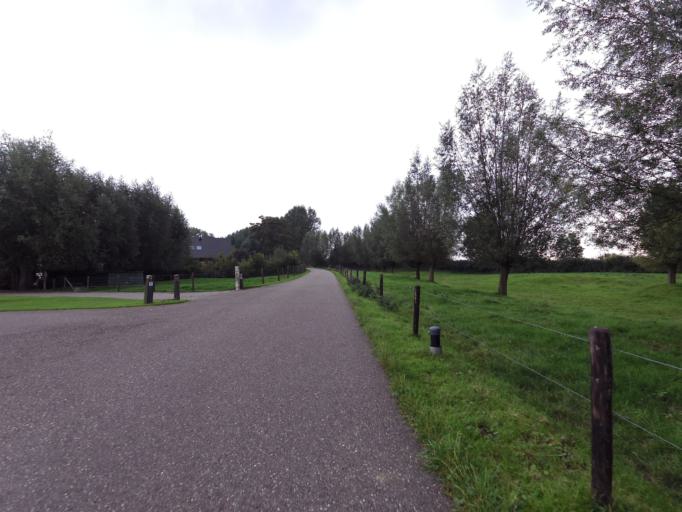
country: NL
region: Gelderland
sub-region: Gemeente Zevenaar
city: Zevenaar
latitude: 51.9094
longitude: 6.0961
